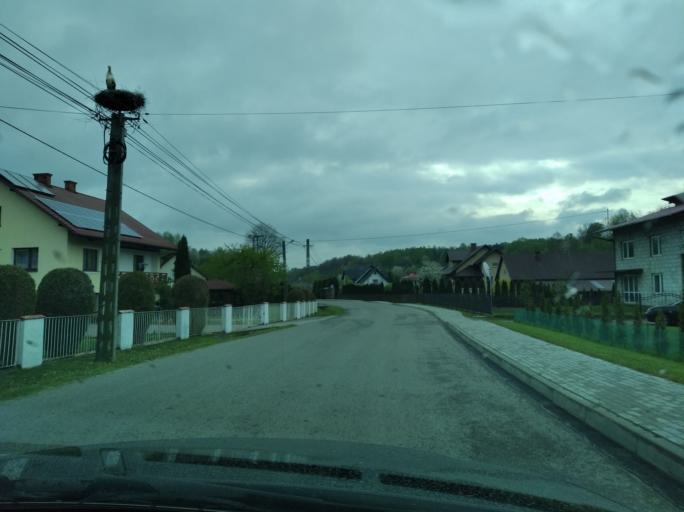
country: PL
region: Subcarpathian Voivodeship
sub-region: Powiat rzeszowski
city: Lecka
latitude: 49.8702
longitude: 22.0320
